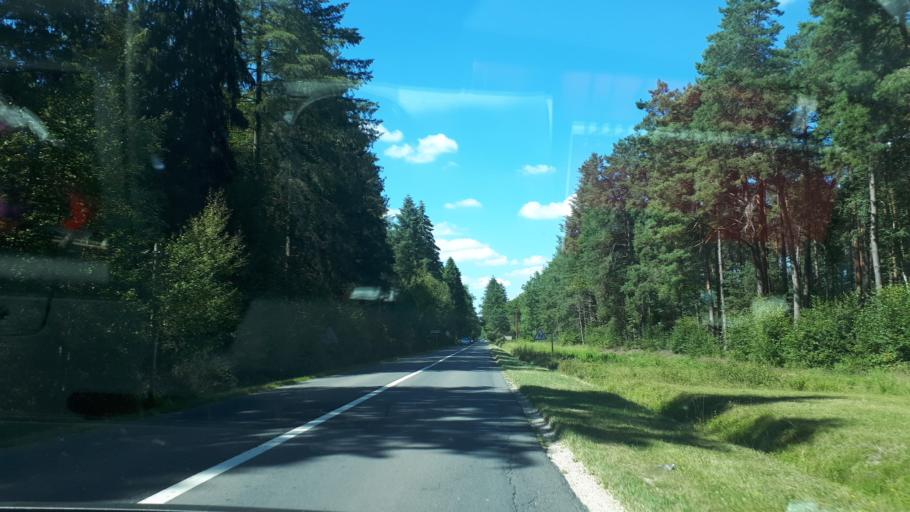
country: FR
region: Centre
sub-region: Departement du Loir-et-Cher
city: Lamotte-Beuvron
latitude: 47.5913
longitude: 2.0100
